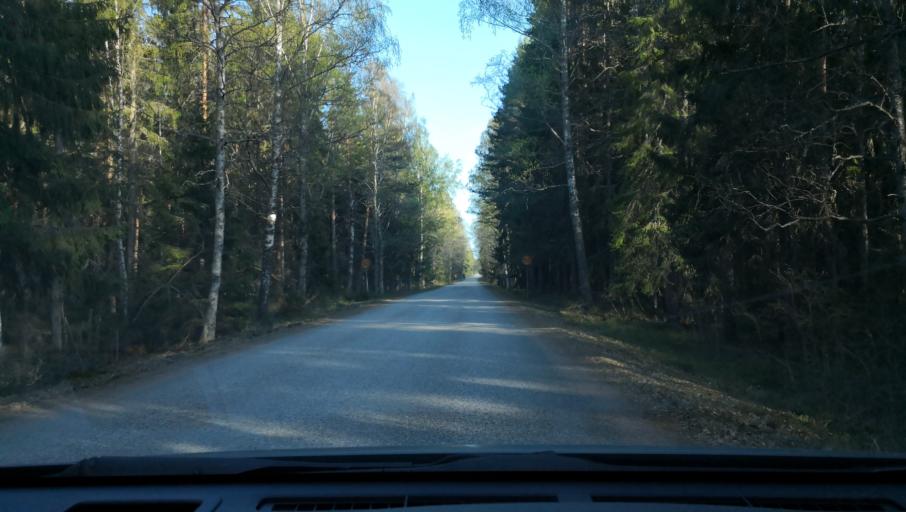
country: SE
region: Uppsala
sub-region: Heby Kommun
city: Tarnsjo
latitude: 60.2728
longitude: 16.9032
